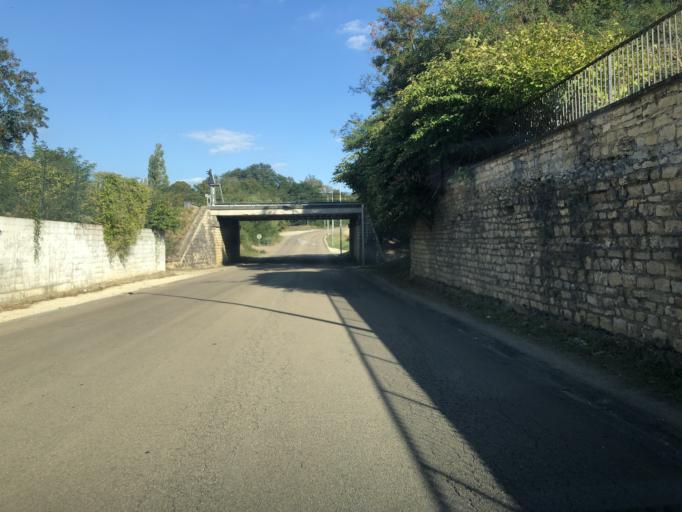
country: FR
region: Bourgogne
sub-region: Departement de l'Yonne
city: Auxerre
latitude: 47.8062
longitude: 3.5863
